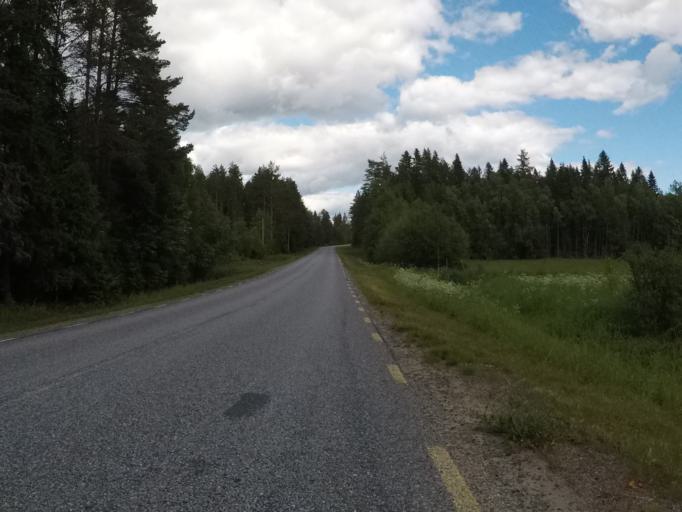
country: SE
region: Vaesterbotten
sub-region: Umea Kommun
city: Saevar
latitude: 63.9502
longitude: 20.7927
